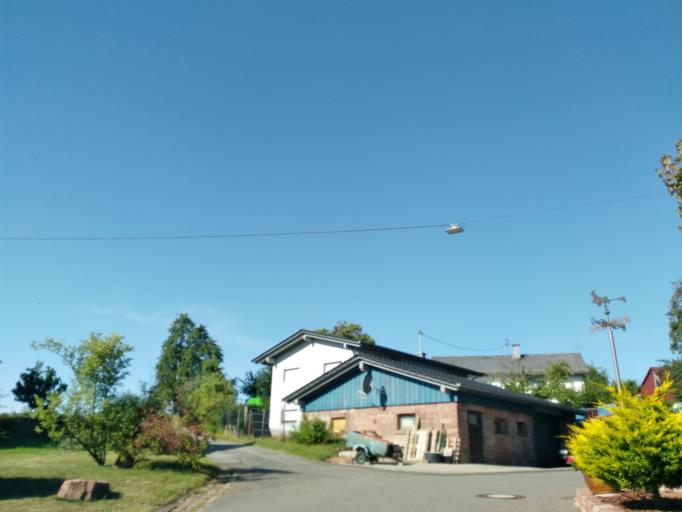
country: DE
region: Baden-Wuerttemberg
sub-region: Karlsruhe Region
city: Mudau
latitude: 49.5147
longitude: 9.1982
